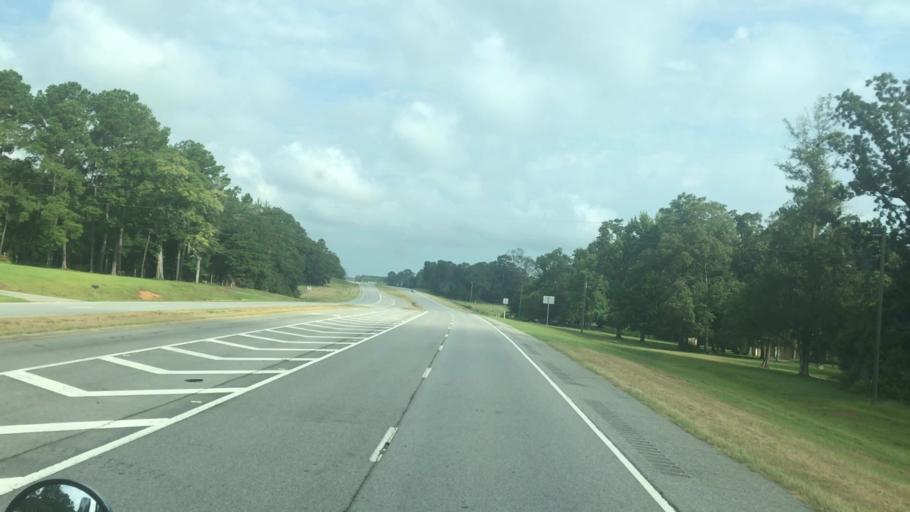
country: US
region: Georgia
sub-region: Miller County
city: Colquitt
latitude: 31.2456
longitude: -84.7921
